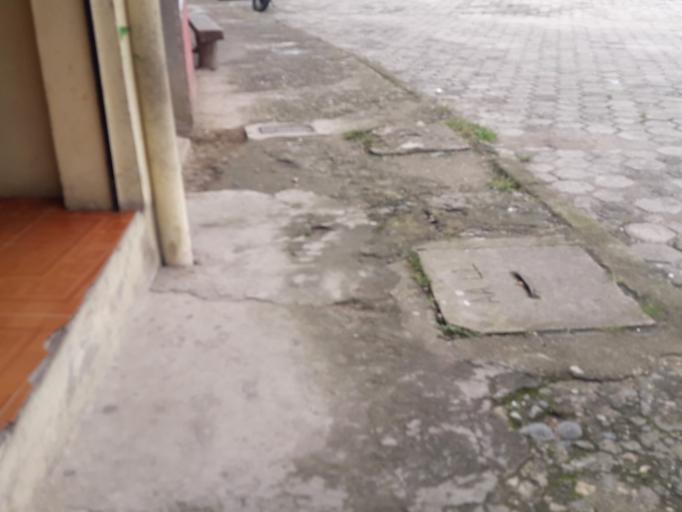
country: EC
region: Napo
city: Tena
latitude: -0.9990
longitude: -77.8147
